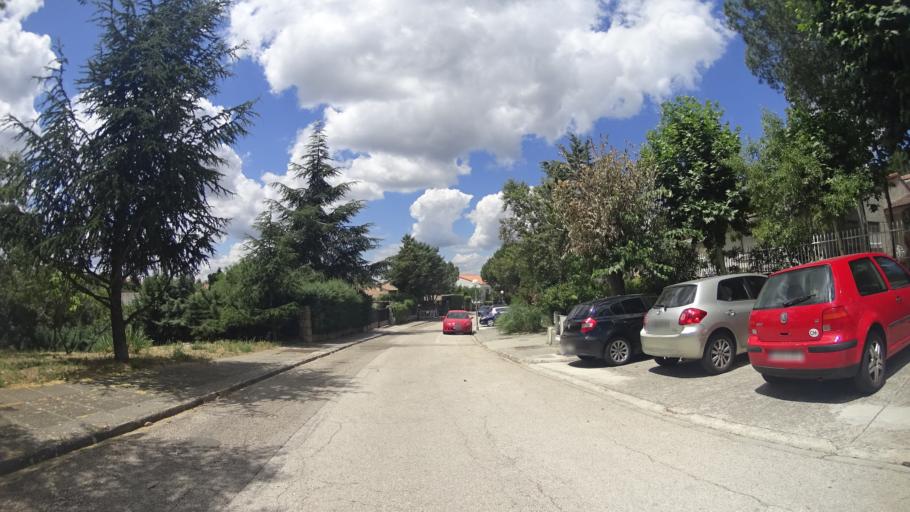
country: ES
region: Madrid
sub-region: Provincia de Madrid
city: Torrelodones
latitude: 40.6060
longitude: -3.9371
